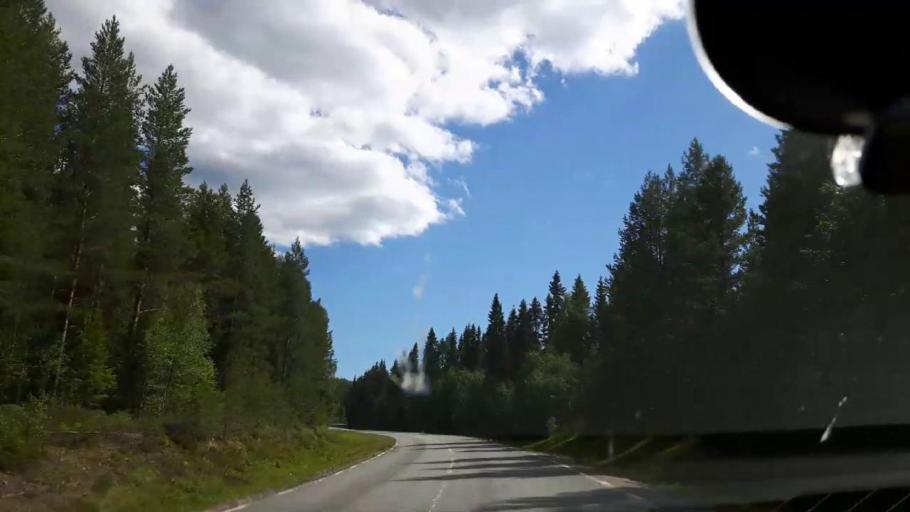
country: SE
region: Vaesternorrland
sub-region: Ange Kommun
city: Fransta
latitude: 62.8152
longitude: 16.2064
